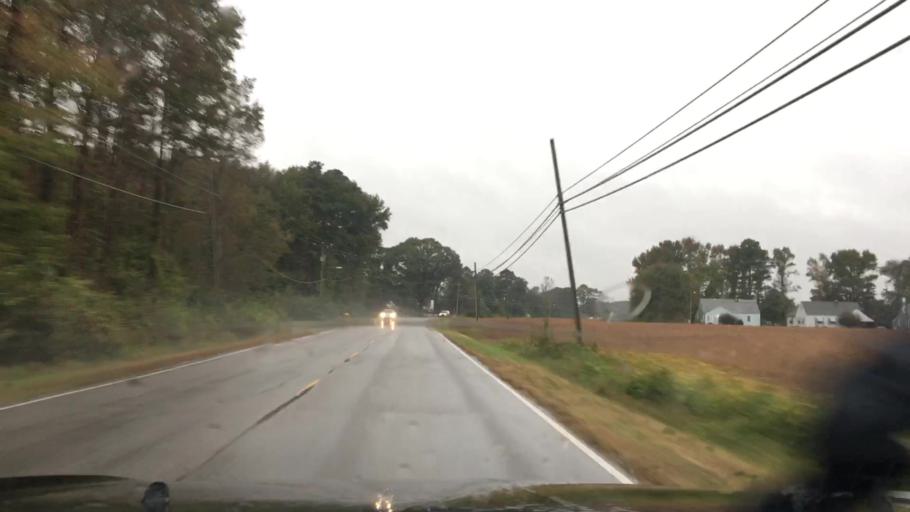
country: US
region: North Carolina
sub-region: Currituck County
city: Moyock
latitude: 36.6651
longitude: -76.2262
